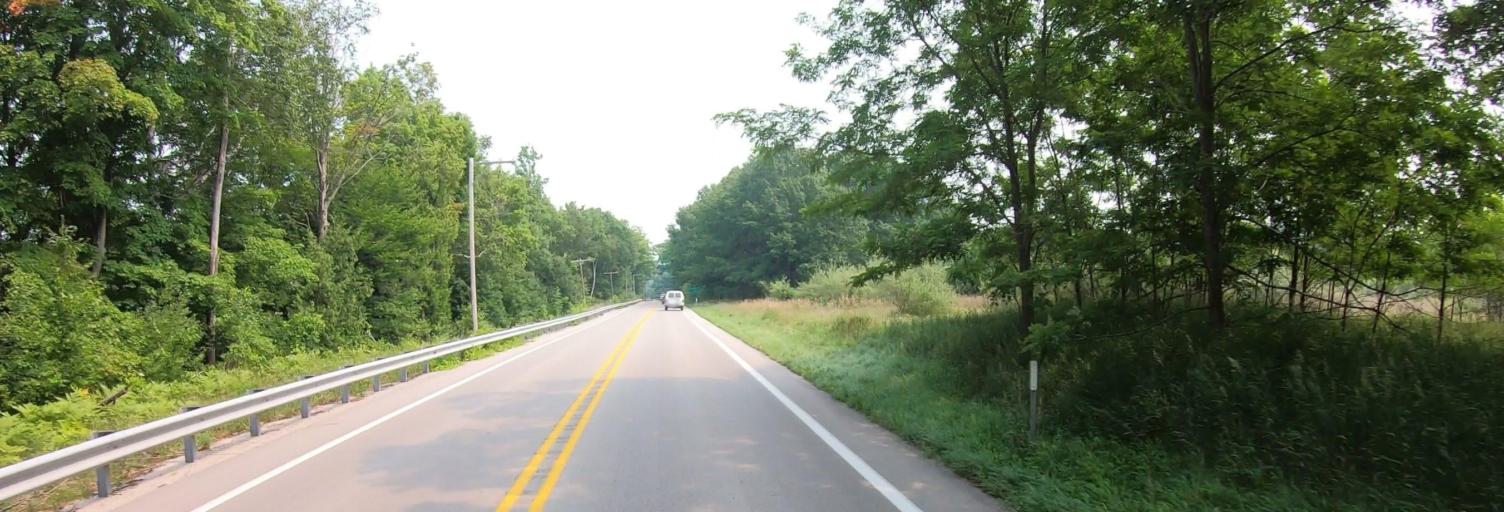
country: US
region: Michigan
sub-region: Leelanau County
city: Leland
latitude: 44.9415
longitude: -85.8053
